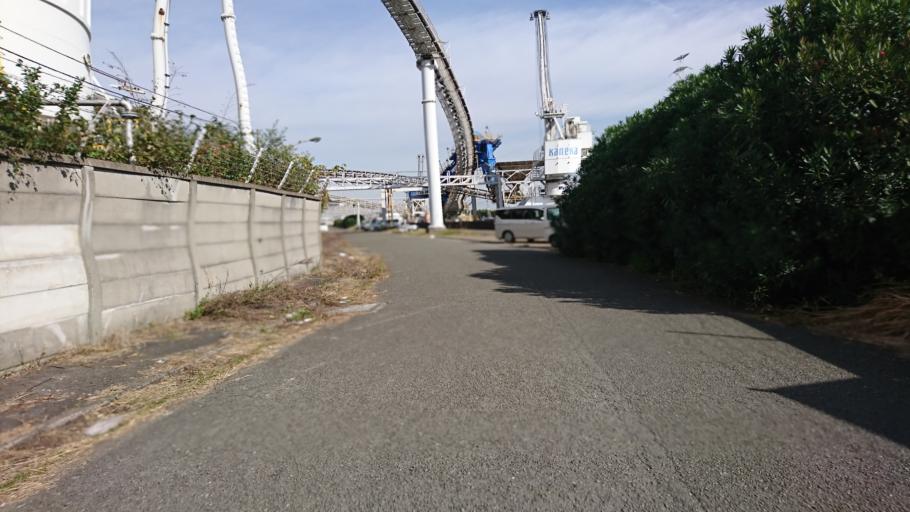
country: JP
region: Hyogo
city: Kakogawacho-honmachi
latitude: 34.7334
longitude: 134.7976
